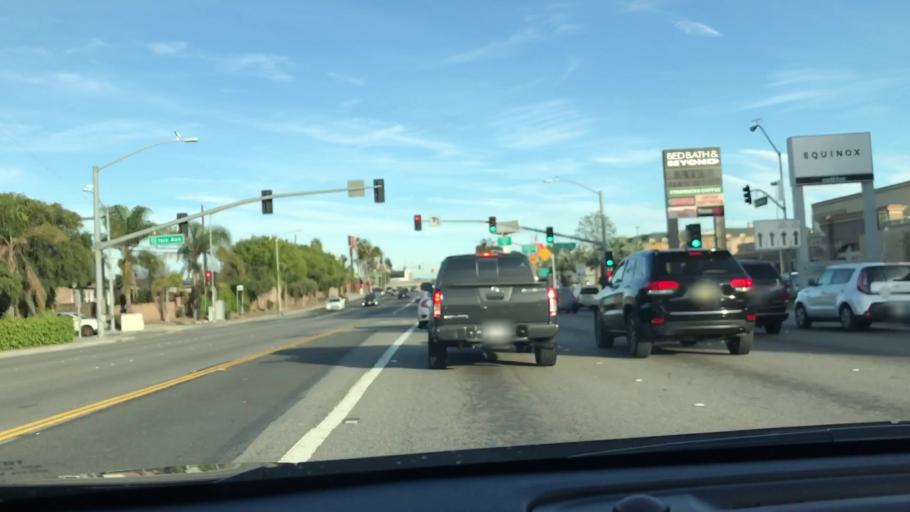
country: US
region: California
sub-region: Los Angeles County
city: Del Aire
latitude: 33.9018
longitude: -118.3750
